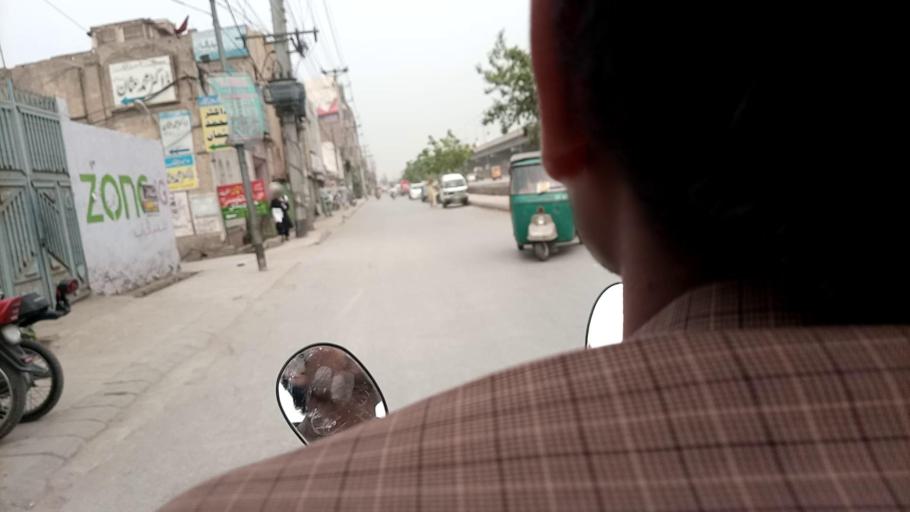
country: PK
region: Khyber Pakhtunkhwa
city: Peshawar
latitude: 34.0157
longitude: 71.5876
